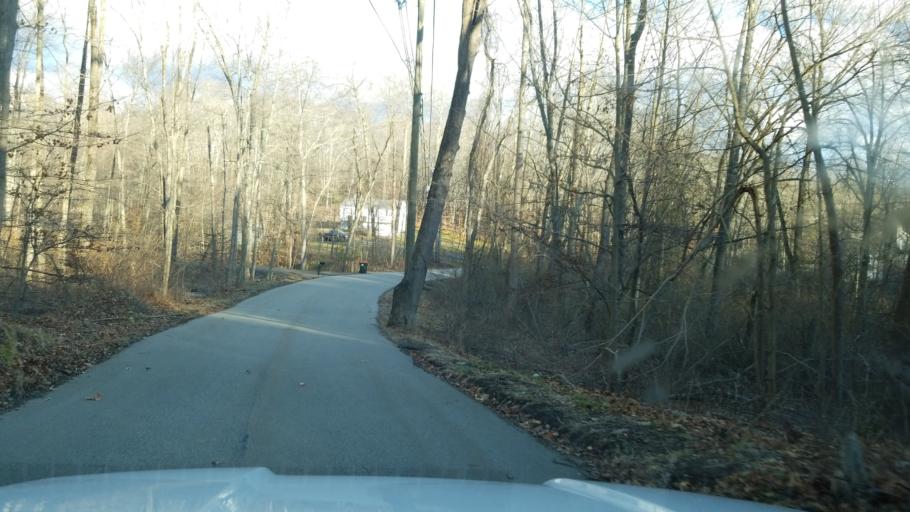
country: US
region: Connecticut
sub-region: Middlesex County
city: Durham
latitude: 41.5124
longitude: -72.6415
